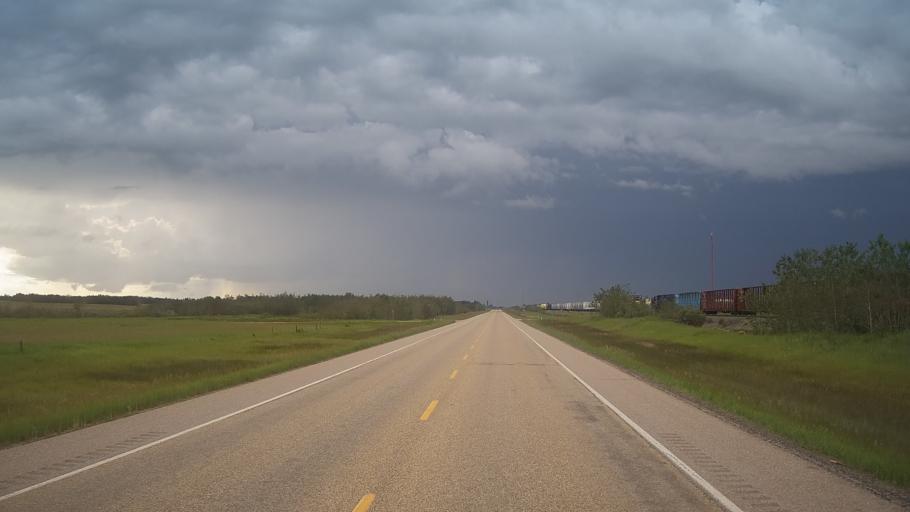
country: CA
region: Alberta
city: Tofield
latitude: 53.2757
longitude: -112.3898
